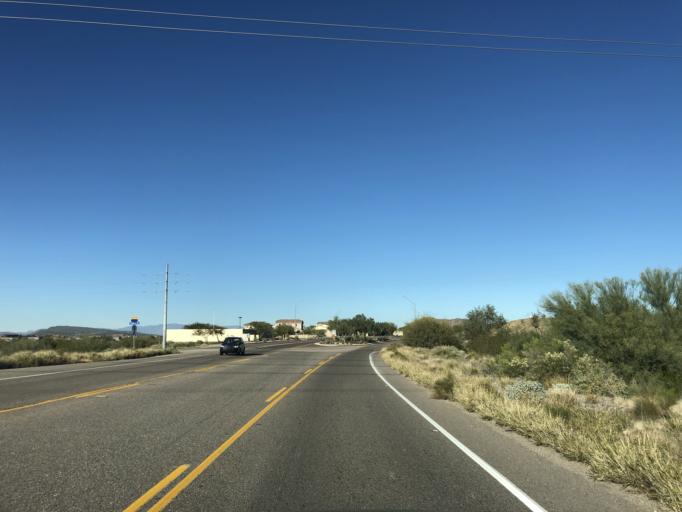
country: US
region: Arizona
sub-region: Maricopa County
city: Sun City West
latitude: 33.7062
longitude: -112.2896
